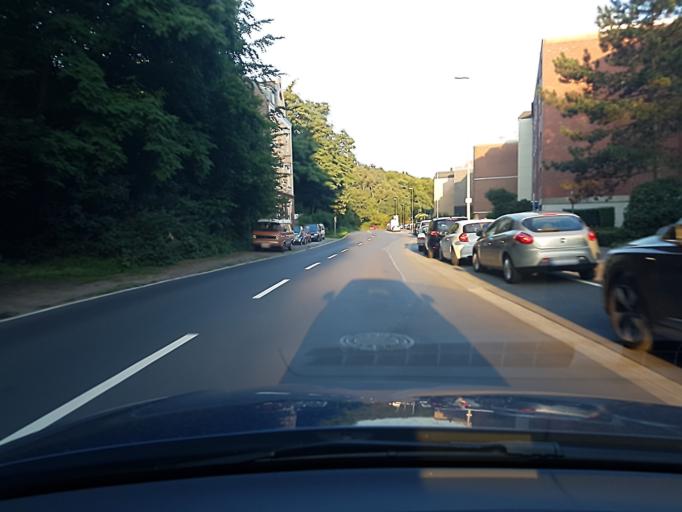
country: DE
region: North Rhine-Westphalia
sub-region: Regierungsbezirk Dusseldorf
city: Ratingen
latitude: 51.2346
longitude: 6.8453
